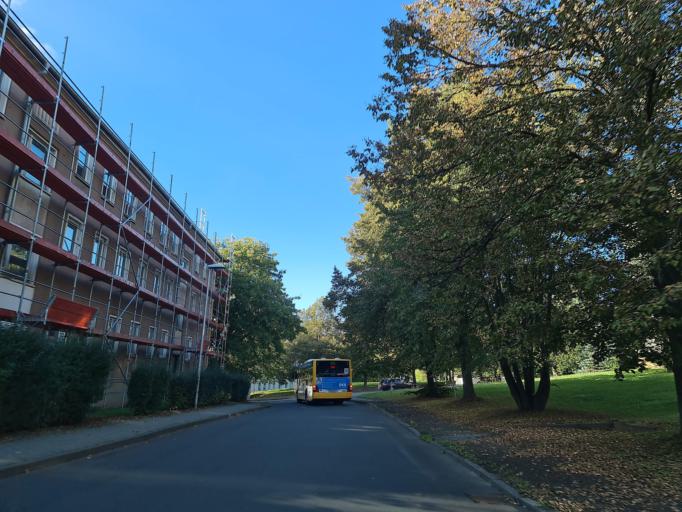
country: DE
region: Thuringia
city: Gera
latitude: 50.8992
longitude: 12.0831
